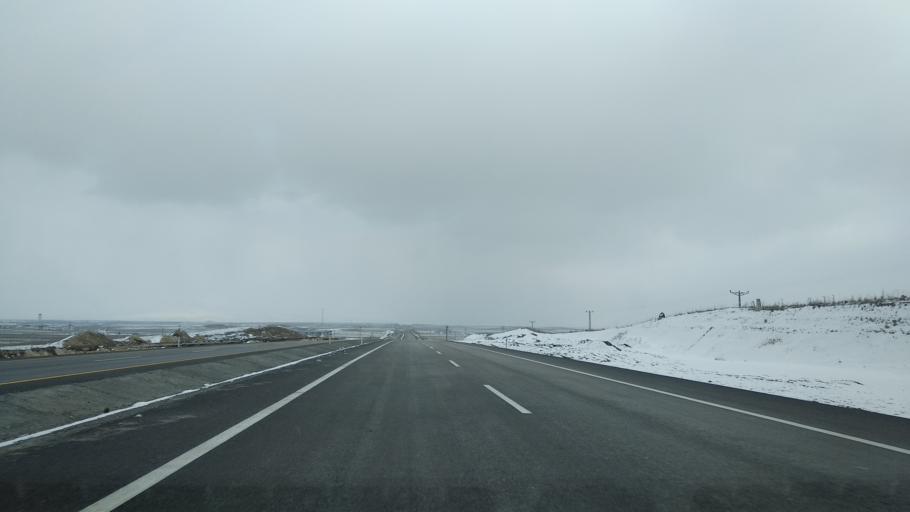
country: TR
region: Kayseri
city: Elbasi
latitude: 38.6534
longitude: 36.0079
